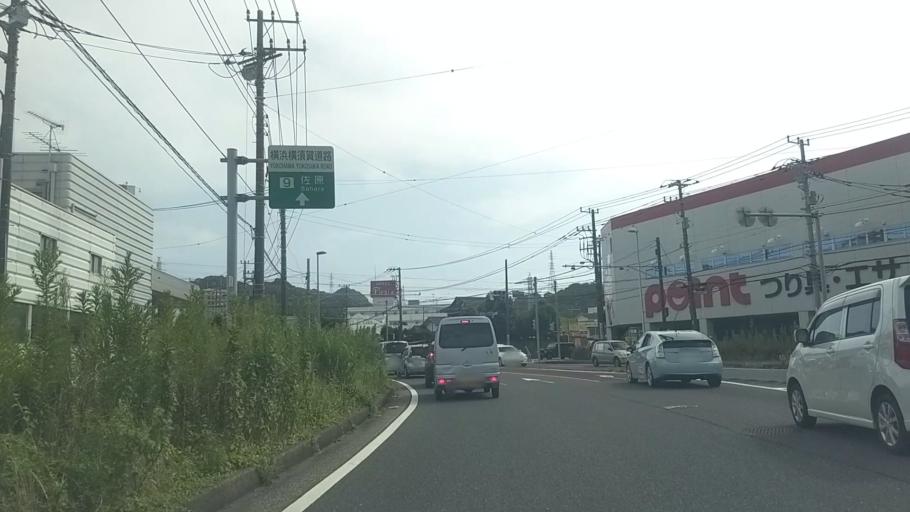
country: JP
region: Kanagawa
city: Yokosuka
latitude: 35.2425
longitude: 139.6808
